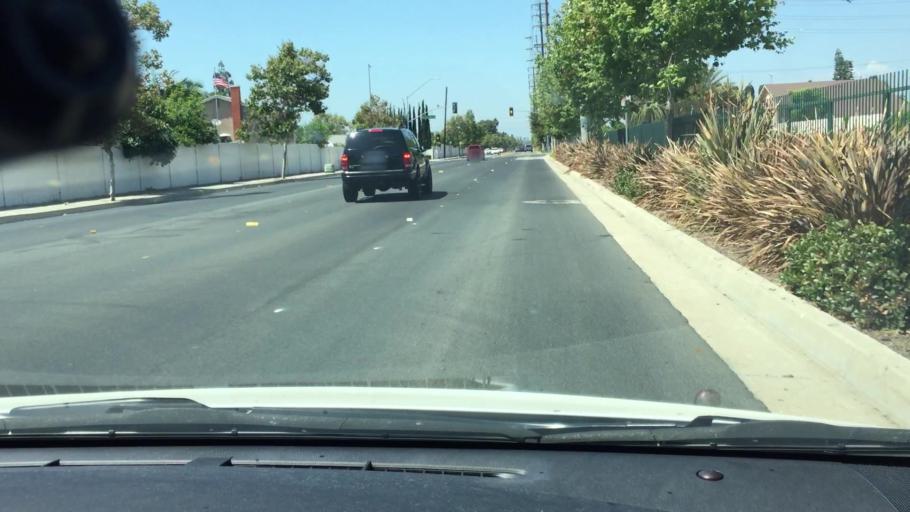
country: US
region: California
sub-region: Orange County
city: Santa Ana
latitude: 33.6988
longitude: -117.8769
